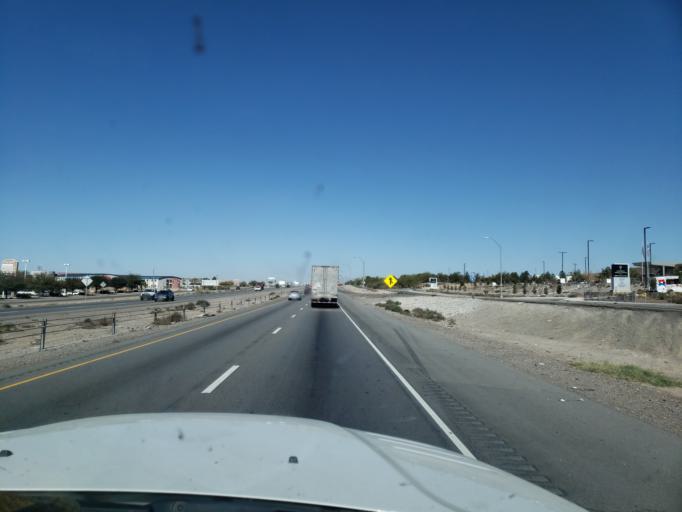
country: US
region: Texas
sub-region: El Paso County
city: Canutillo
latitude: 31.8919
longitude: -106.5827
